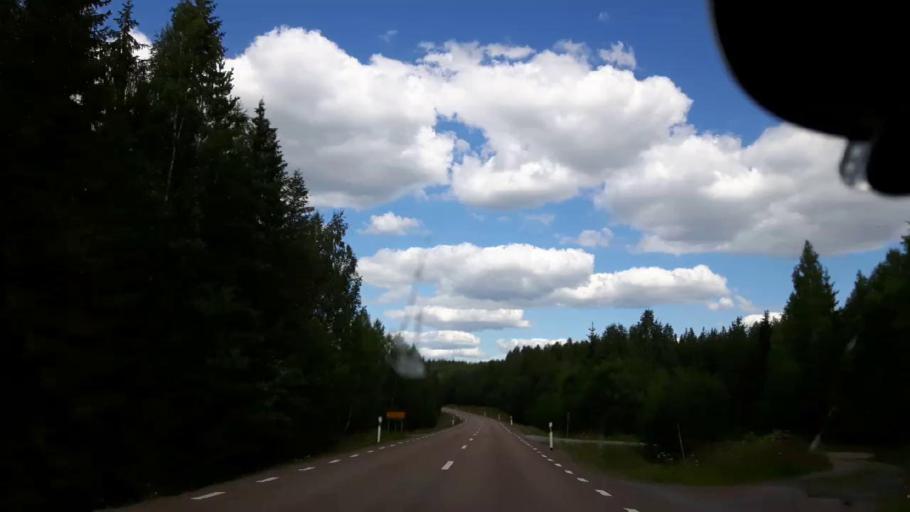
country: SE
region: Jaemtland
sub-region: Ragunda Kommun
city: Hammarstrand
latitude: 62.9163
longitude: 16.7036
